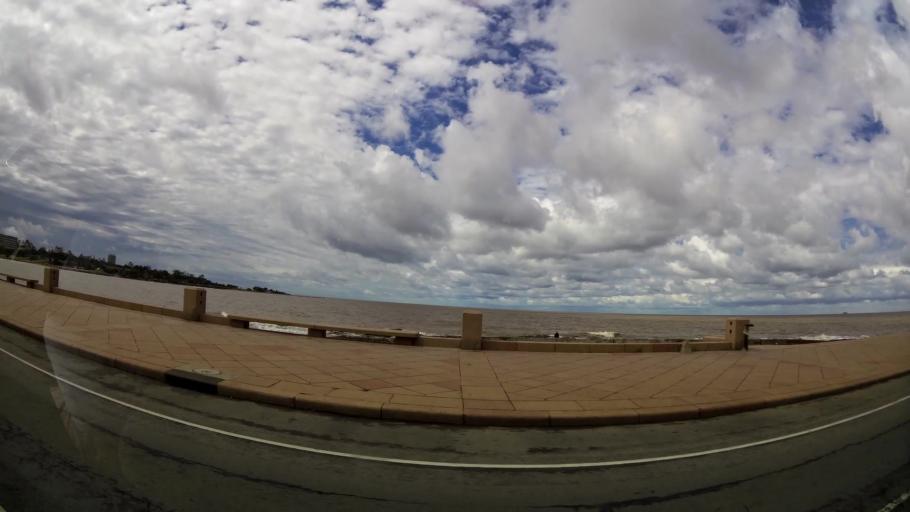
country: UY
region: Montevideo
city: Montevideo
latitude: -34.9146
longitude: -56.1785
